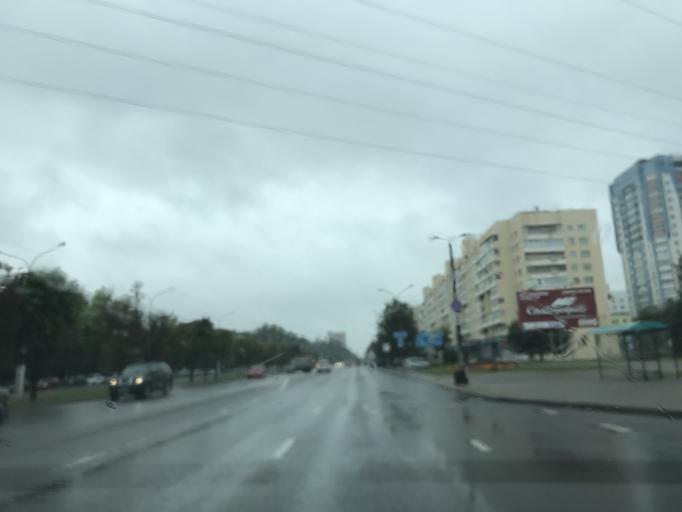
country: BY
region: Minsk
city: Minsk
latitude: 53.9496
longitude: 27.6154
